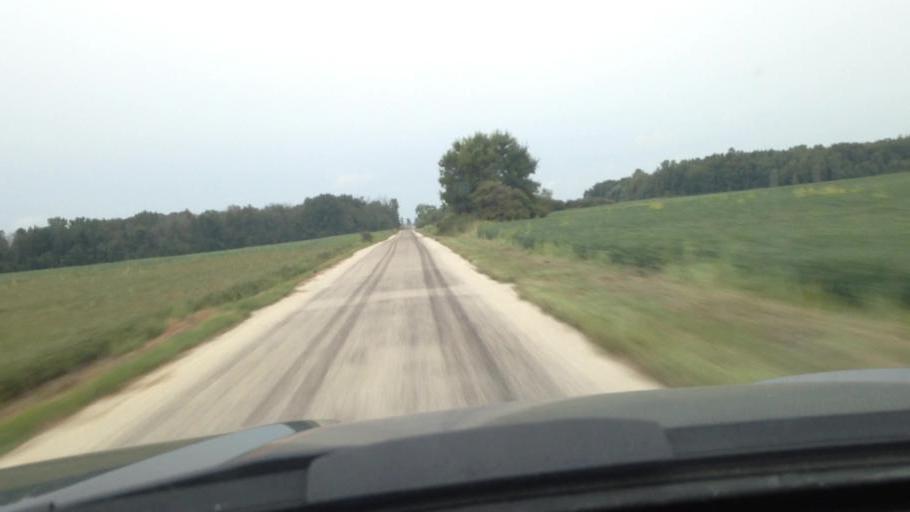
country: US
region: Indiana
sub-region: Randolph County
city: Union City
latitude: 40.2196
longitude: -84.8615
